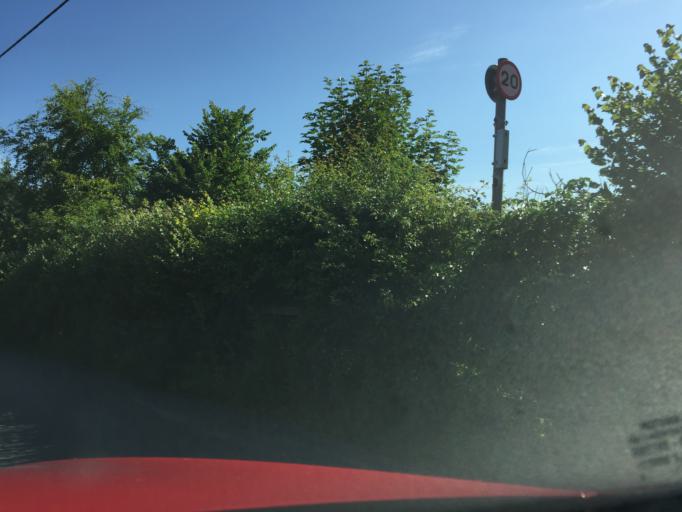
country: GB
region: England
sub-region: Gloucestershire
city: Stonehouse
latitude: 51.7555
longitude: -2.2514
